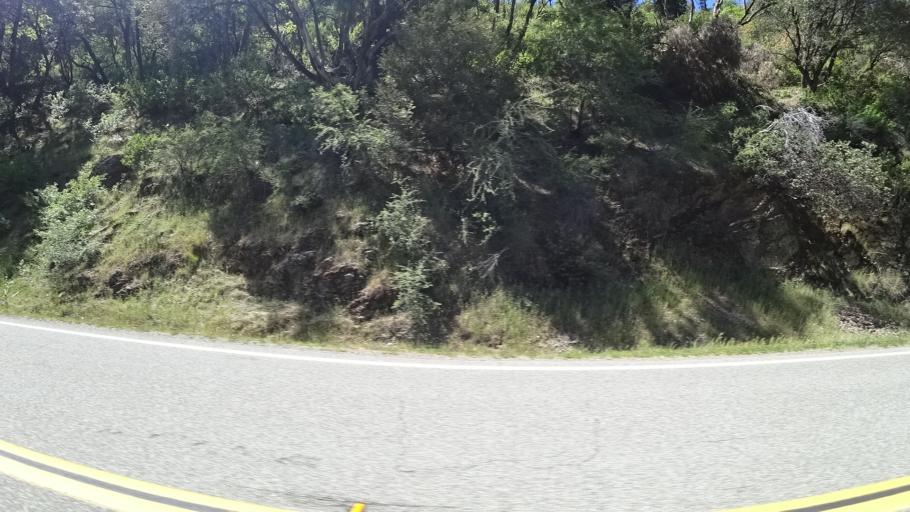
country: US
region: California
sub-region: Trinity County
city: Weaverville
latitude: 40.7607
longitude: -123.1486
